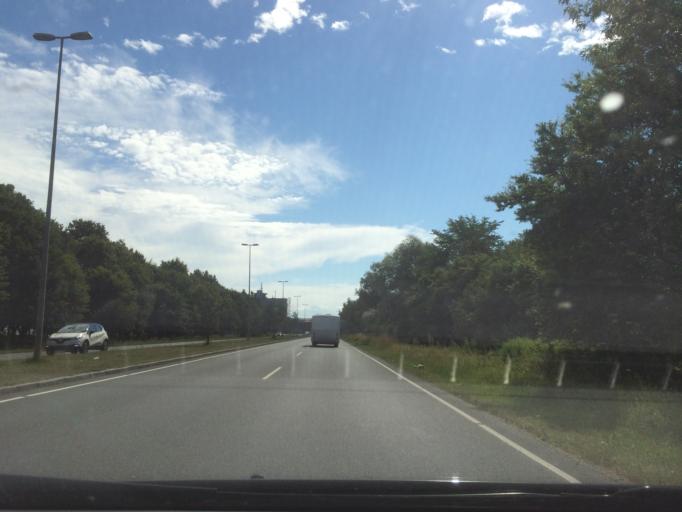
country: DK
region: Zealand
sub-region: Koge Kommune
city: Koge
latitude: 55.4816
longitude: 12.1810
